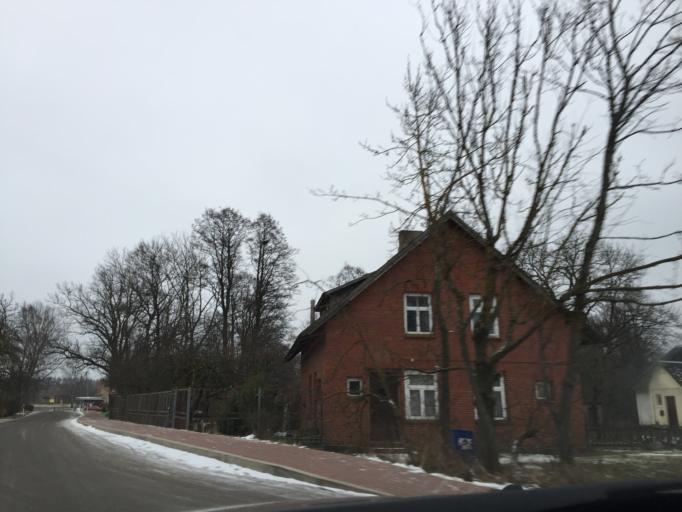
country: LV
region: Saulkrastu
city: Saulkrasti
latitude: 57.4906
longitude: 24.3893
